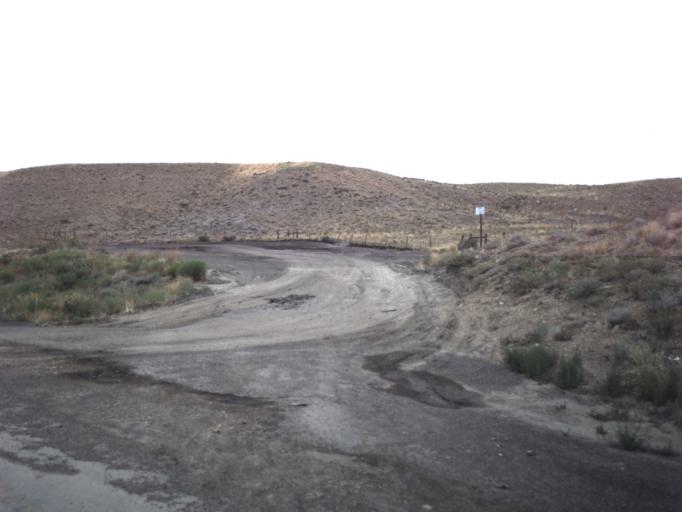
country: US
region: Utah
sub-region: Carbon County
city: East Carbon City
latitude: 39.4744
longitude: -110.5029
